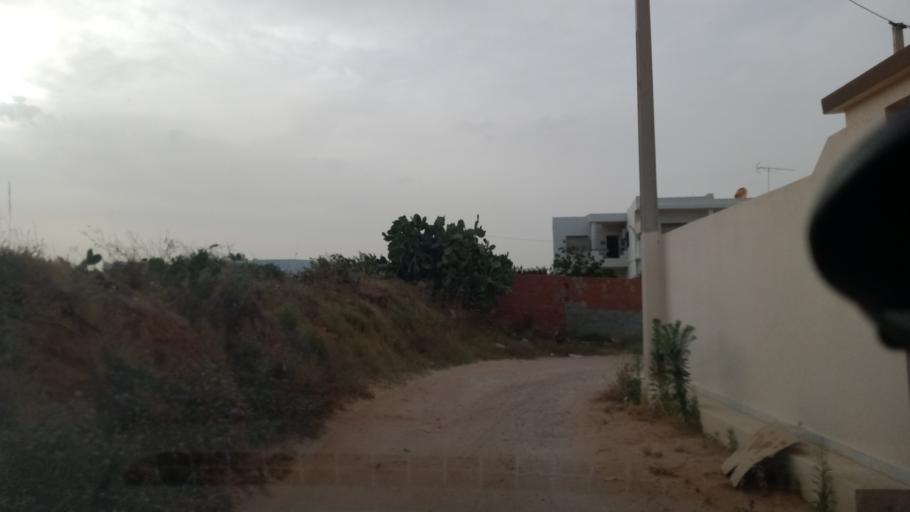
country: TN
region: Safaqis
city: Al Qarmadah
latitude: 34.7893
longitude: 10.7641
